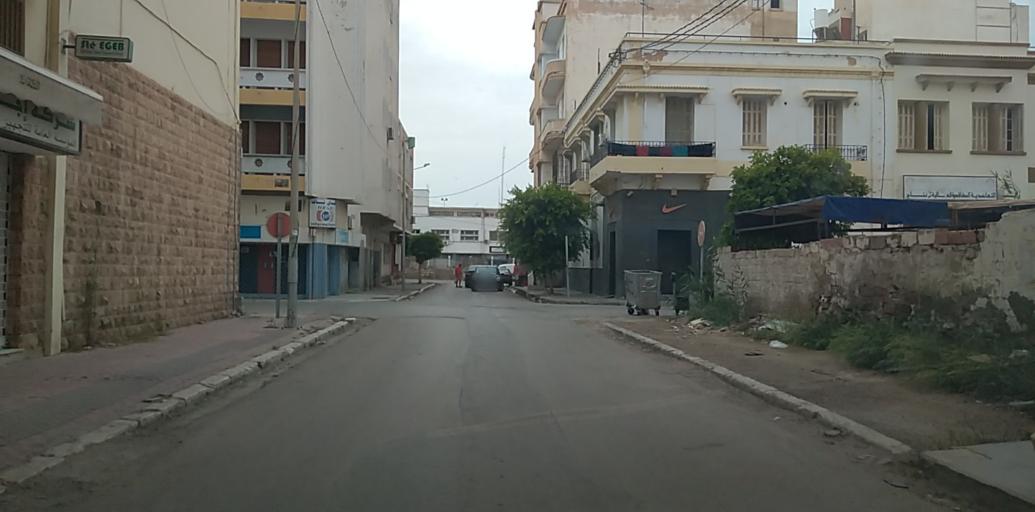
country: TN
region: Safaqis
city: Sfax
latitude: 34.7300
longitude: 10.7644
